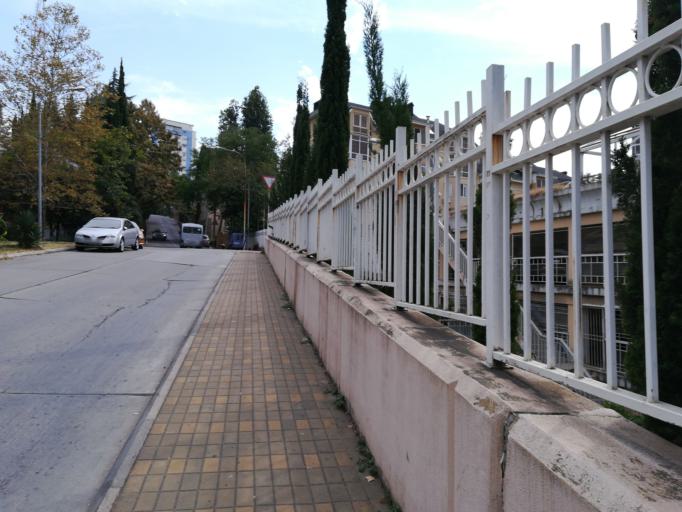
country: RU
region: Krasnodarskiy
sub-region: Sochi City
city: Sochi
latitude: 43.5922
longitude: 39.7353
